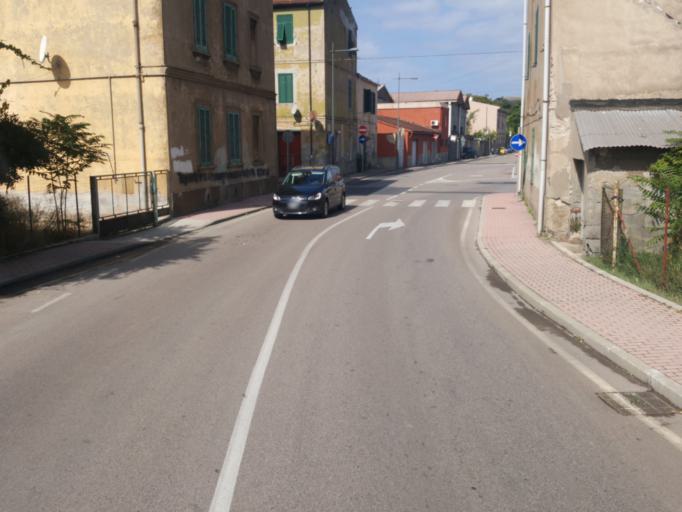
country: IT
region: Tuscany
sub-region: Provincia di Livorno
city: Piombino
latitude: 42.9261
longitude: 10.5349
